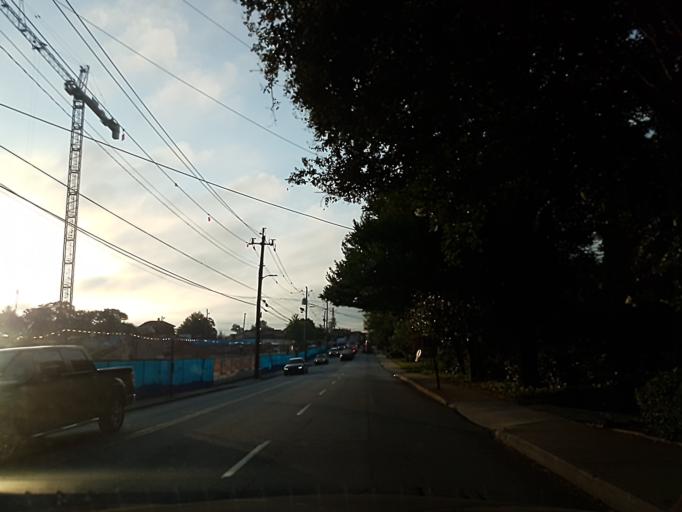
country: US
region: Georgia
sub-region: Fulton County
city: Atlanta
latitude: 33.8076
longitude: -84.3957
